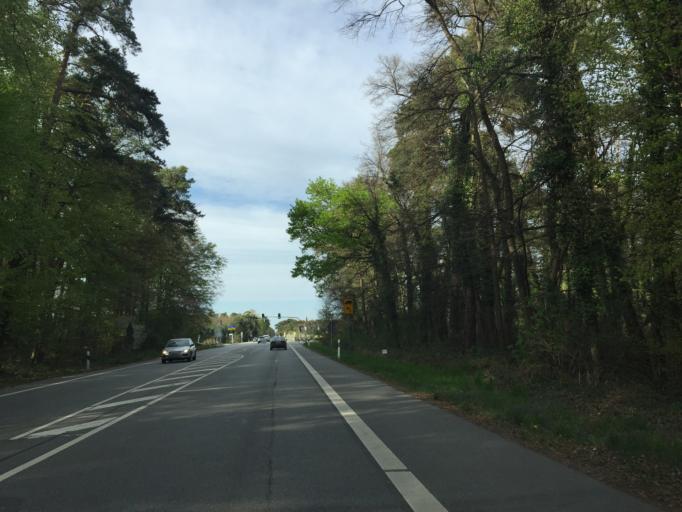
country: DE
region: Hesse
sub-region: Regierungsbezirk Darmstadt
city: Bickenbach
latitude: 49.7669
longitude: 8.6230
